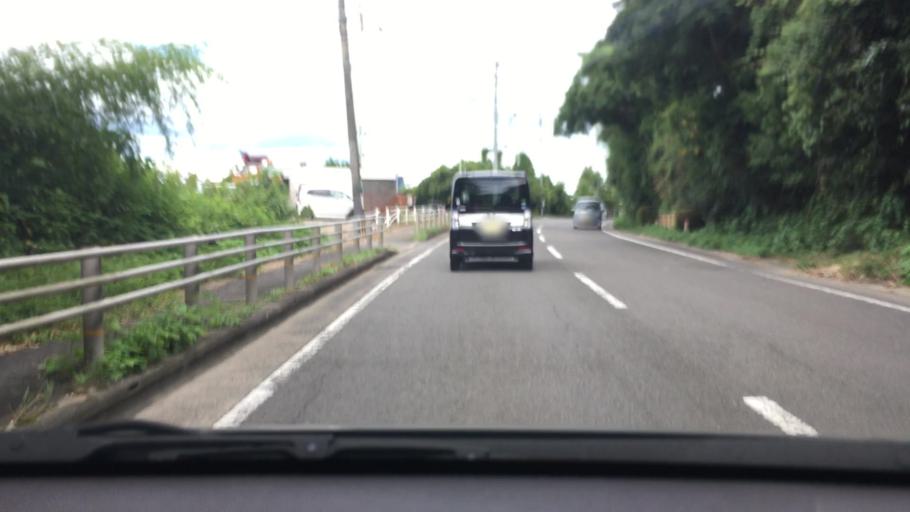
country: JP
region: Nagasaki
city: Togitsu
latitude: 32.8609
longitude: 129.8105
